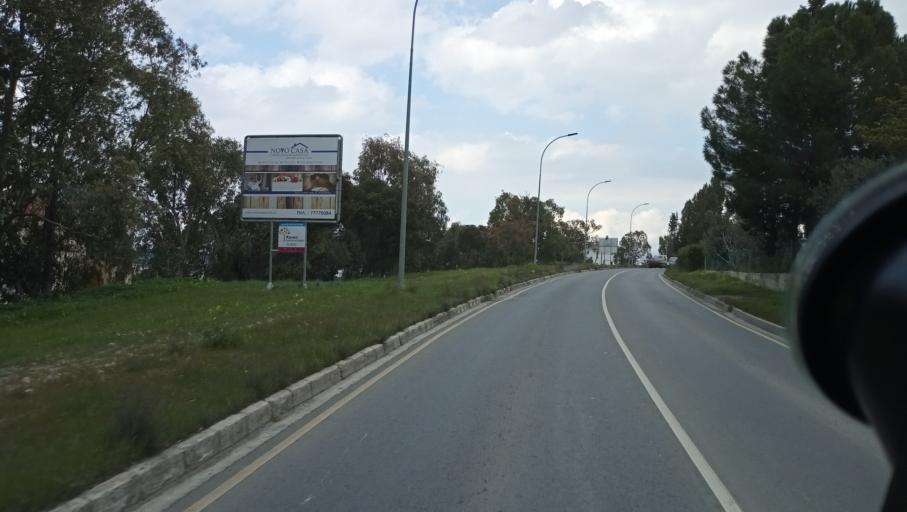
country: CY
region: Lefkosia
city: Kato Deftera
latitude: 35.1398
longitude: 33.3013
